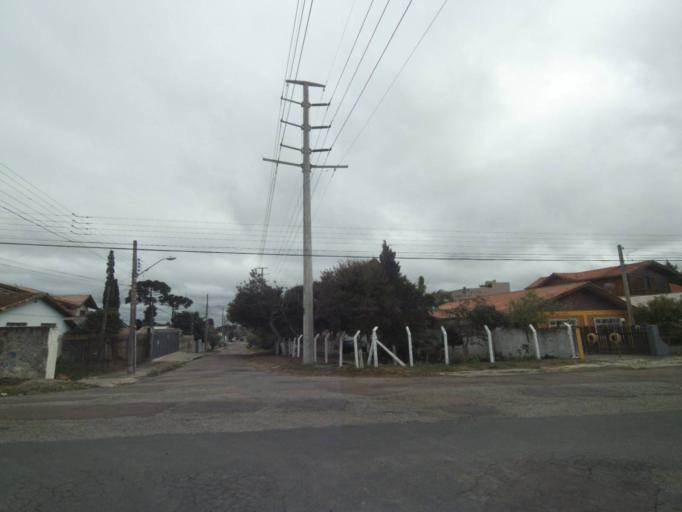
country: BR
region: Parana
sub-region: Sao Jose Dos Pinhais
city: Sao Jose dos Pinhais
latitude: -25.5241
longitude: -49.2985
